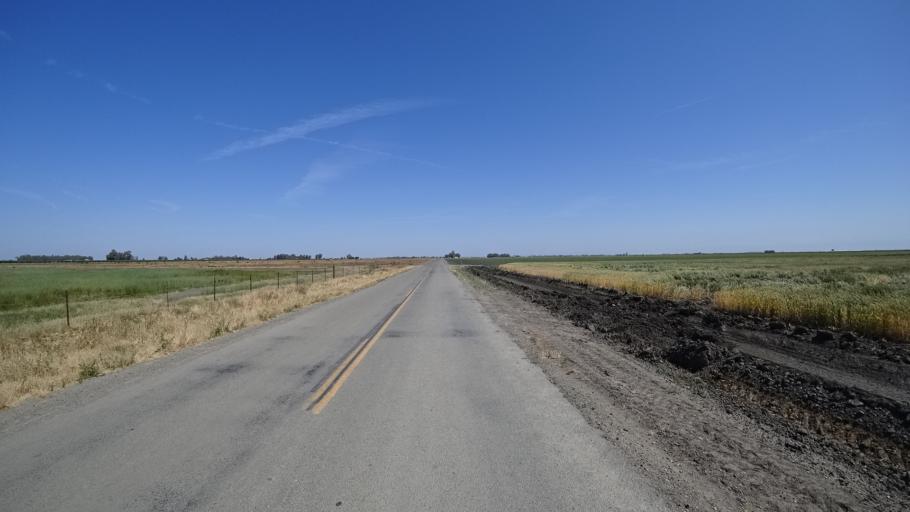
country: US
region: California
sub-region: Kings County
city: Stratford
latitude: 36.1811
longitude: -119.7803
